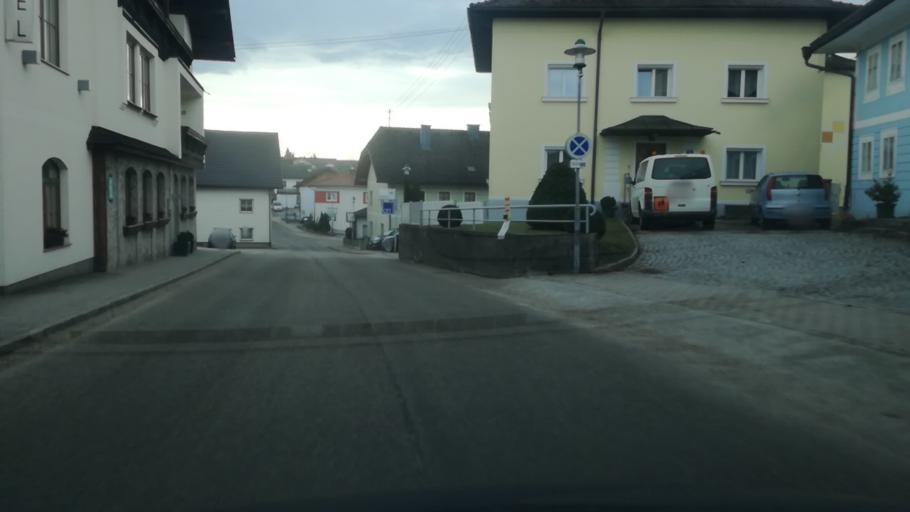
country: AT
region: Upper Austria
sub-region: Politischer Bezirk Vocklabruck
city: Neukirchen an der Vockla
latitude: 48.0407
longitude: 13.5386
